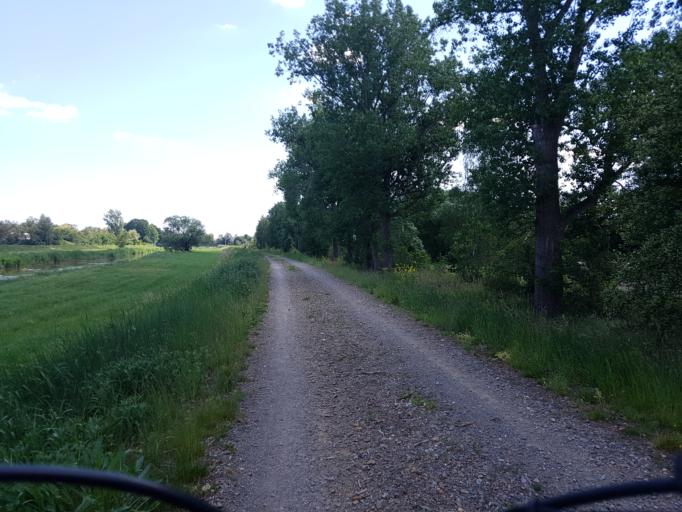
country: DE
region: Brandenburg
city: Bad Liebenwerda
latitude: 51.5250
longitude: 13.3847
